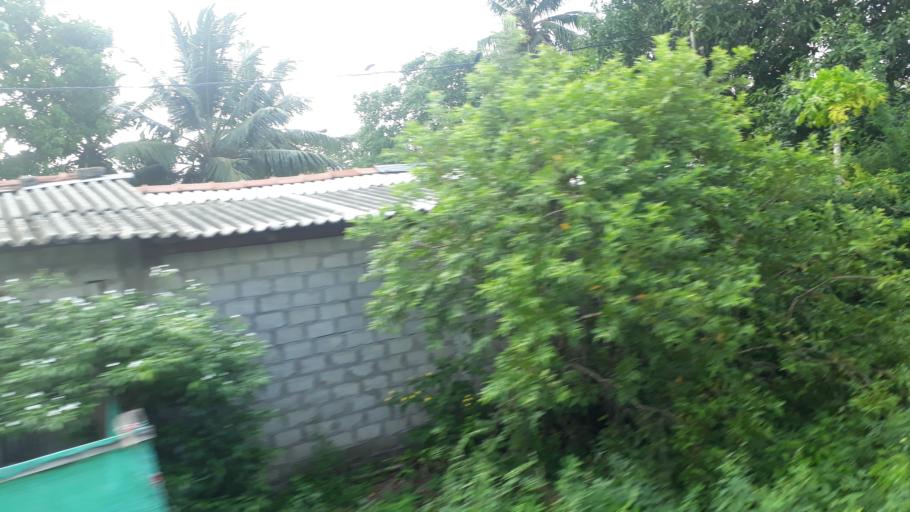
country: LK
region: Western
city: Kolonnawa
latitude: 6.9500
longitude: 79.8883
